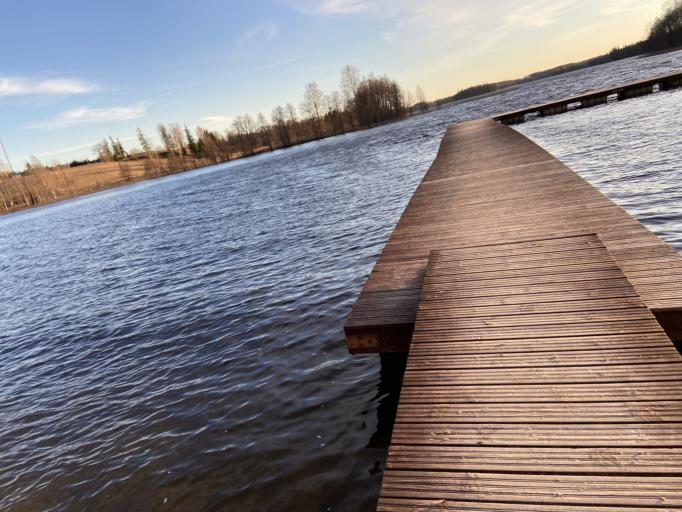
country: EE
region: Tartu
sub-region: Elva linn
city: Elva
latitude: 58.0430
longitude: 26.4688
